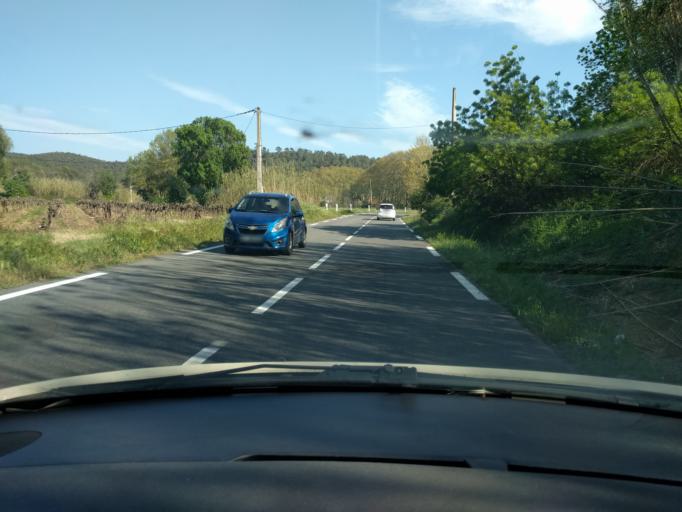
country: FR
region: Provence-Alpes-Cote d'Azur
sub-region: Departement du Var
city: Hyeres
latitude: 43.1613
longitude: 6.1247
